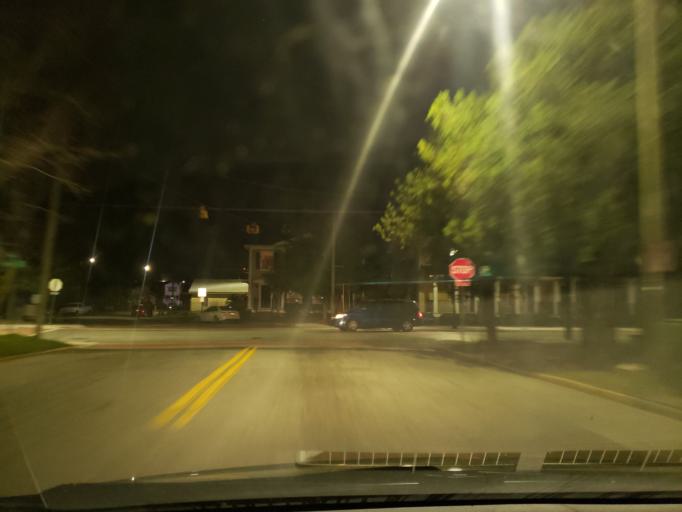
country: US
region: Georgia
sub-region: Chatham County
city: Savannah
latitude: 32.0631
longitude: -81.0804
